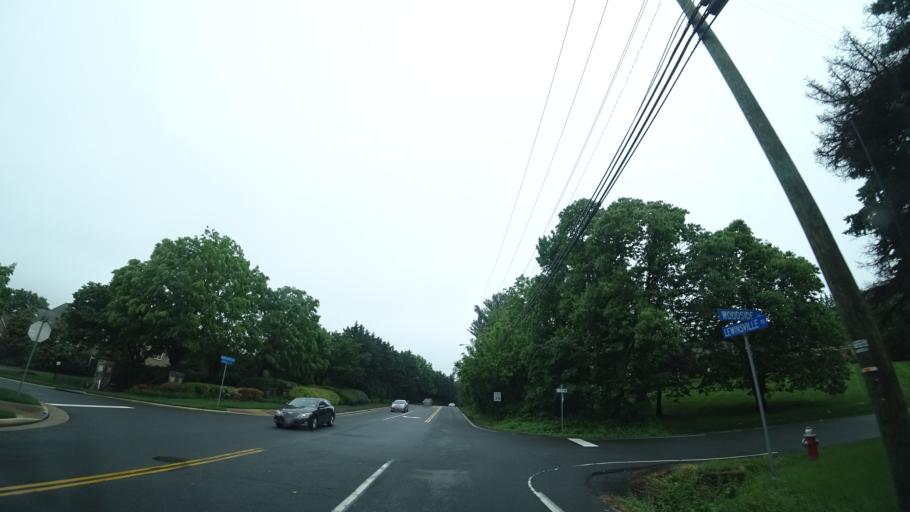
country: US
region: Virginia
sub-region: Fairfax County
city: Tysons Corner
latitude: 38.9418
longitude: -77.2497
